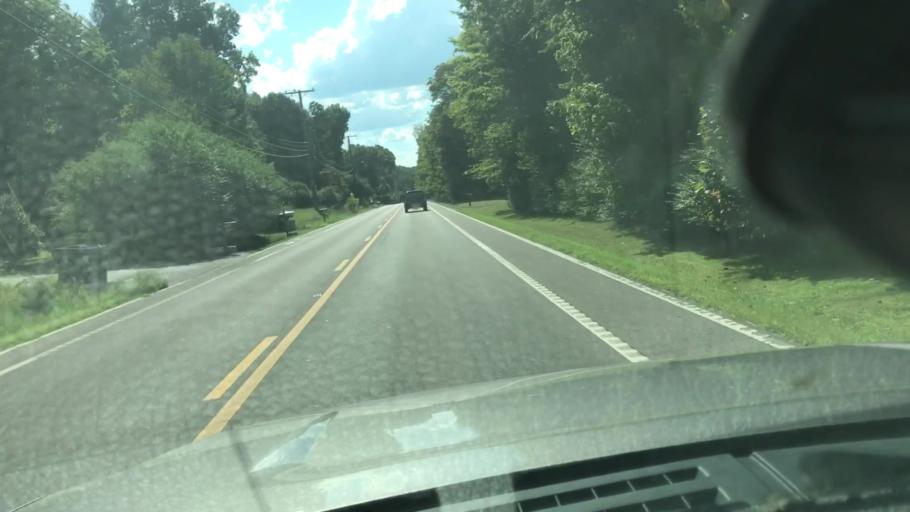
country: US
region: Tennessee
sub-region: Cheatham County
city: Pegram
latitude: 36.0283
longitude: -87.0063
